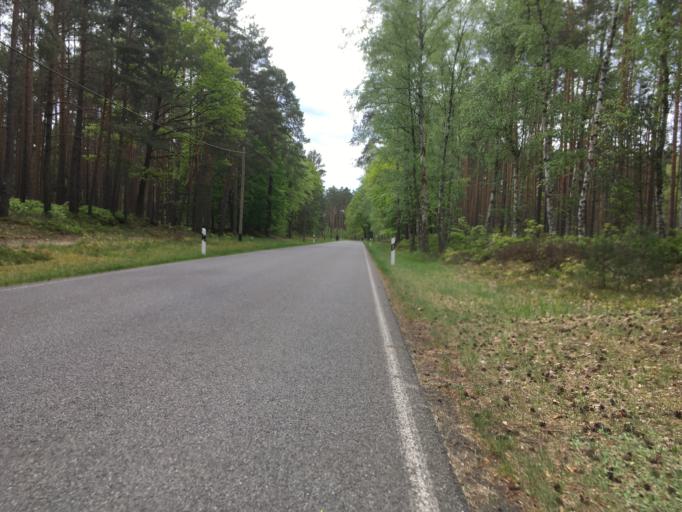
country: DE
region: Brandenburg
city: Joachimsthal
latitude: 52.9965
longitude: 13.7431
